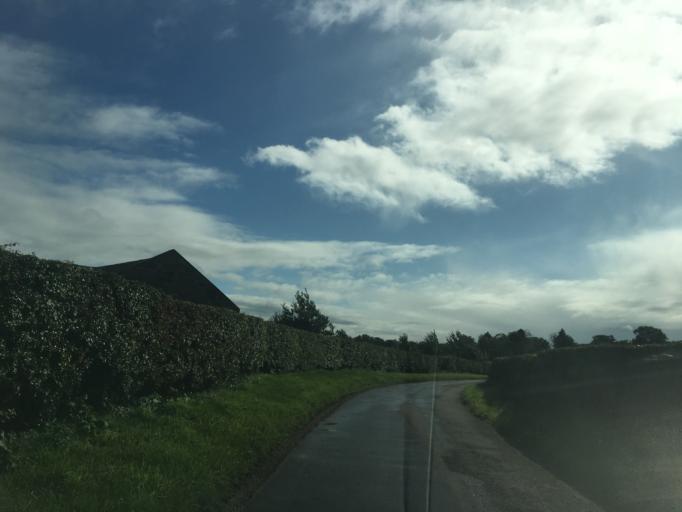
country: GB
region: Scotland
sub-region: Edinburgh
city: Kirkliston
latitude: 55.9601
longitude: -3.3742
